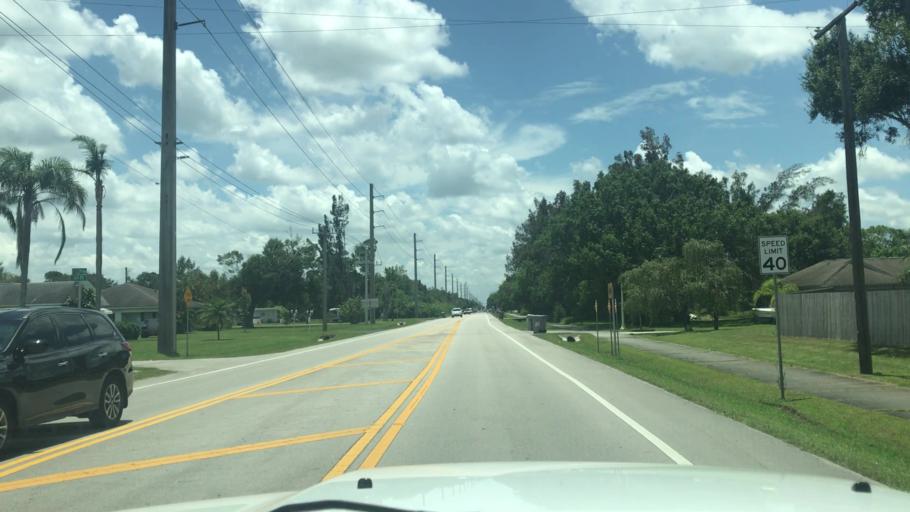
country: US
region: Florida
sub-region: Indian River County
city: Vero Beach South
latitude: 27.6230
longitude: -80.4139
